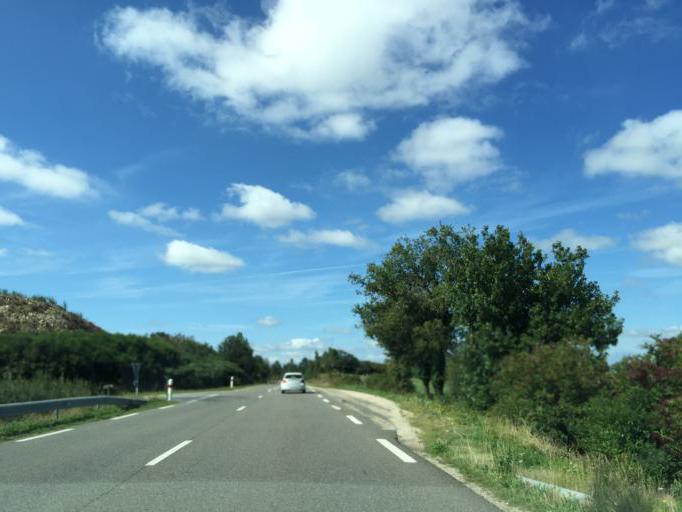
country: FR
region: Midi-Pyrenees
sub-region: Departement de l'Aveyron
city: Rieupeyroux
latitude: 44.3172
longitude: 2.1815
